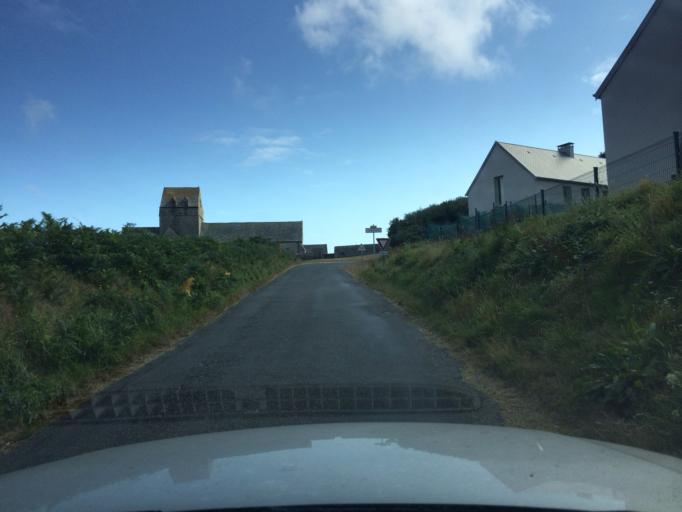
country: FR
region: Lower Normandy
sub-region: Departement de la Manche
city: Beaumont-Hague
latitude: 49.6851
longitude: -1.9044
